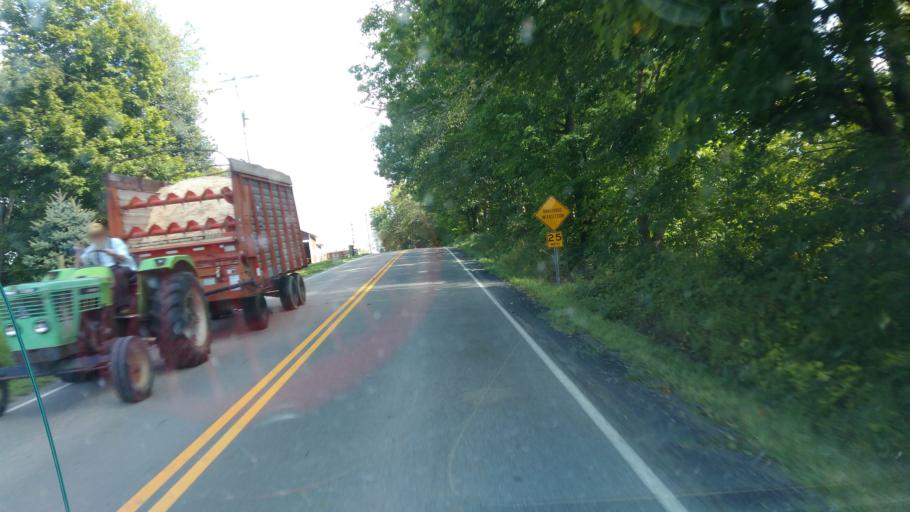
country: US
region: Ohio
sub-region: Holmes County
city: Millersburg
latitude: 40.6201
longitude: -81.8788
